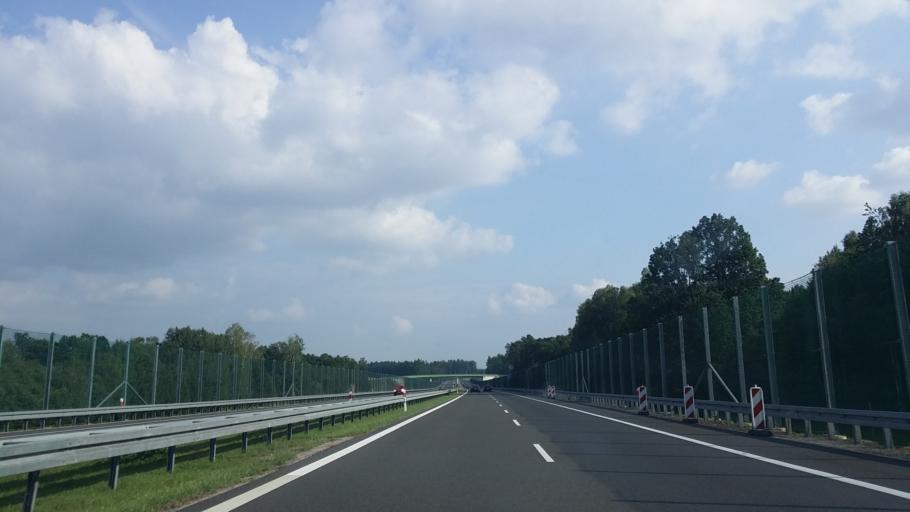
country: PL
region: Lubusz
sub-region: Powiat miedzyrzecki
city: Miedzyrzecz
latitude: 52.5158
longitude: 15.5481
